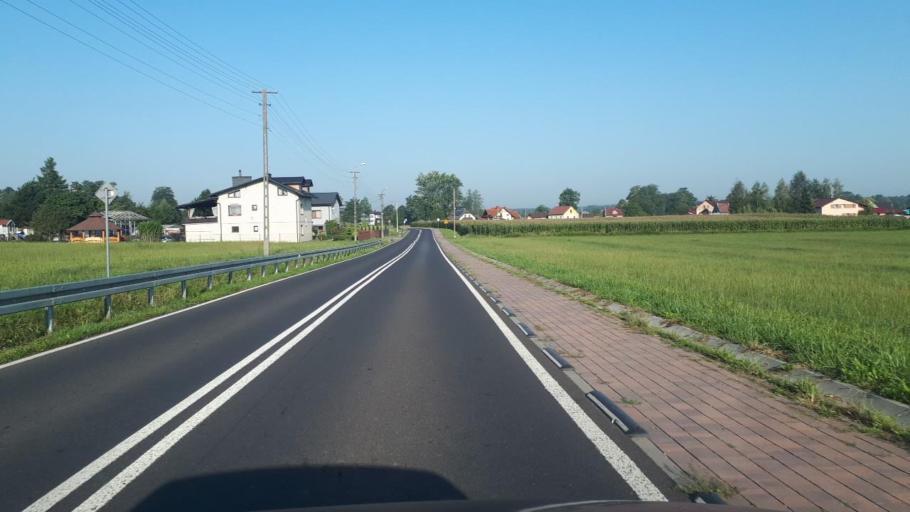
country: PL
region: Silesian Voivodeship
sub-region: Powiat bielski
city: Bronow
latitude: 49.8774
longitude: 18.9105
